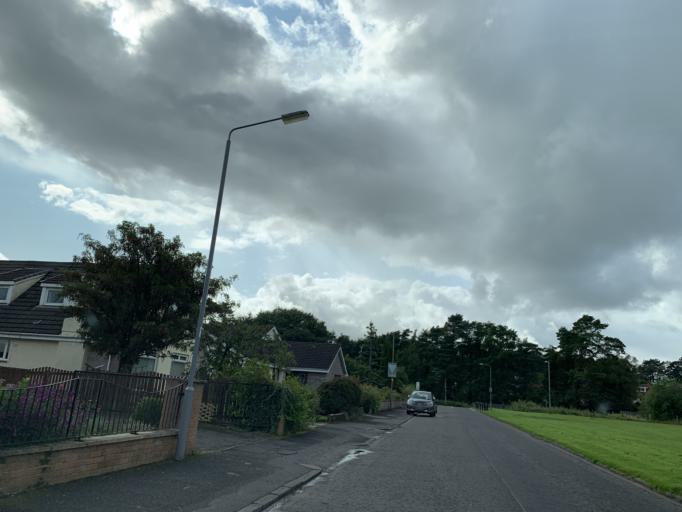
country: GB
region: Scotland
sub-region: East Renfrewshire
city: Newton Mearns
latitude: 55.7848
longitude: -4.3264
